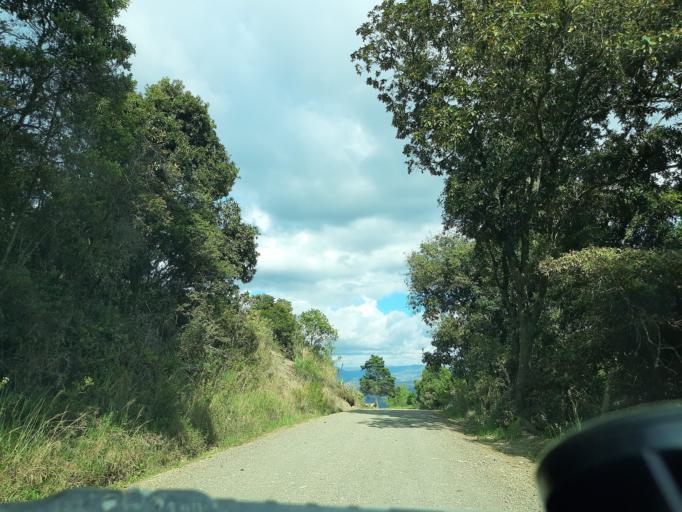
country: CO
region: Boyaca
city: Raquira
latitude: 5.5268
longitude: -73.6693
